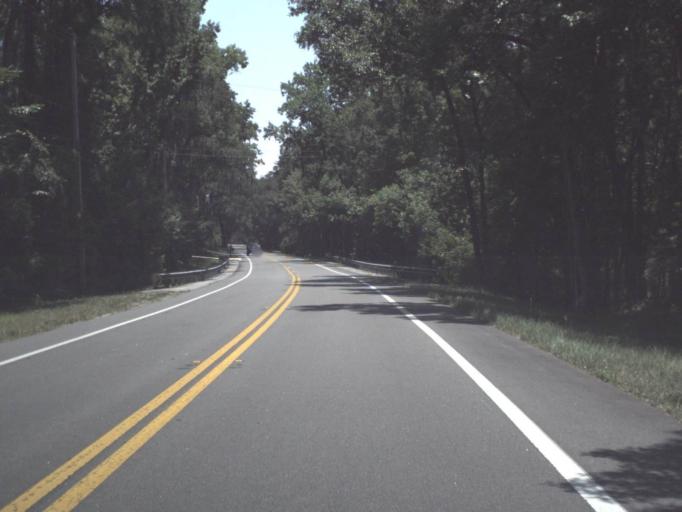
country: US
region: Florida
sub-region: Clay County
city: Green Cove Springs
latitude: 30.0459
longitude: -81.6661
